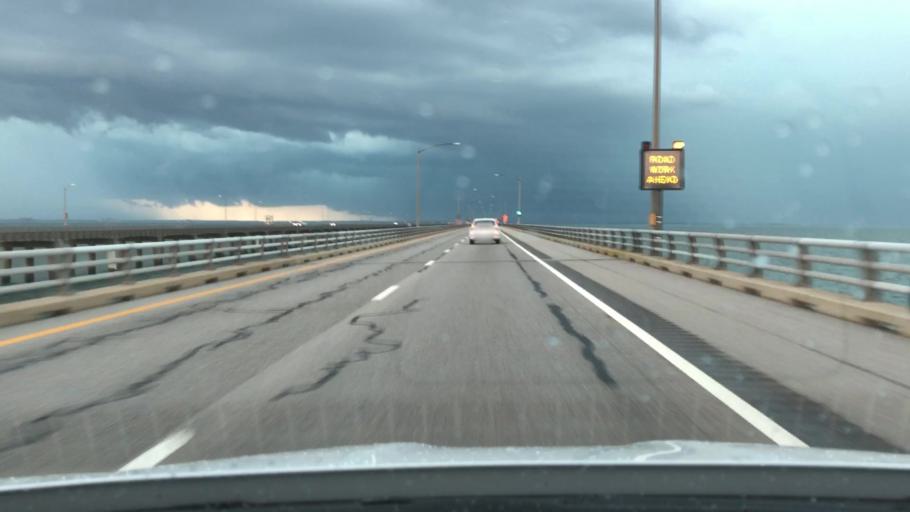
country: US
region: Virginia
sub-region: City of Virginia Beach
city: Virginia Beach
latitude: 36.9997
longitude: -76.0998
